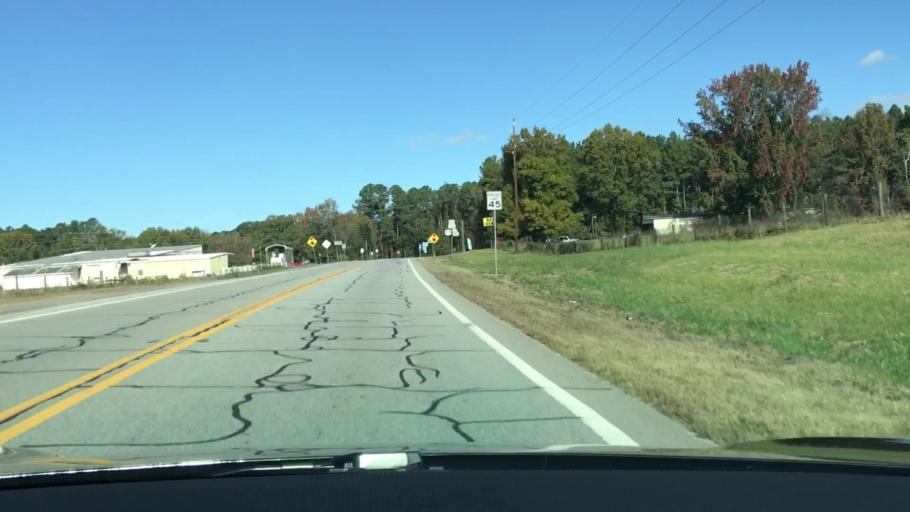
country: US
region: Georgia
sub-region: Warren County
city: Warrenton
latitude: 33.3994
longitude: -82.6547
